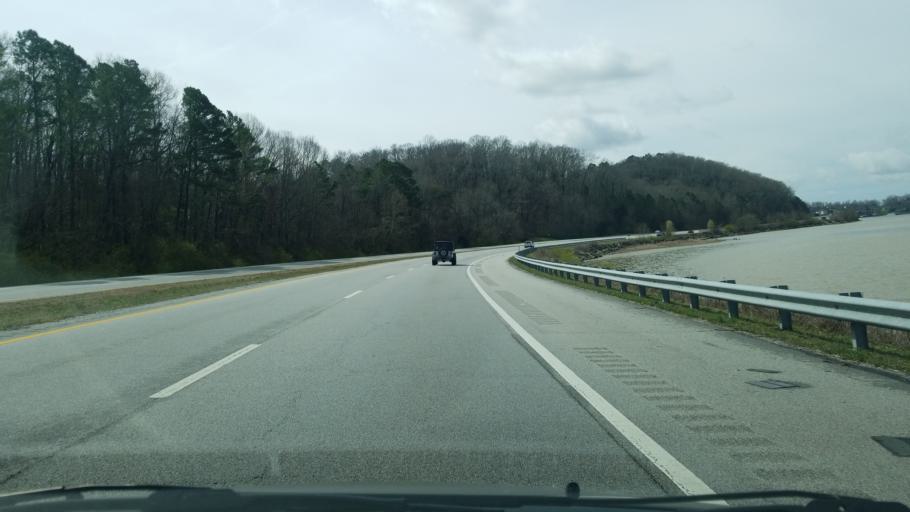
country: US
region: Tennessee
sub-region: Hamilton County
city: Harrison
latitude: 35.1474
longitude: -85.1102
